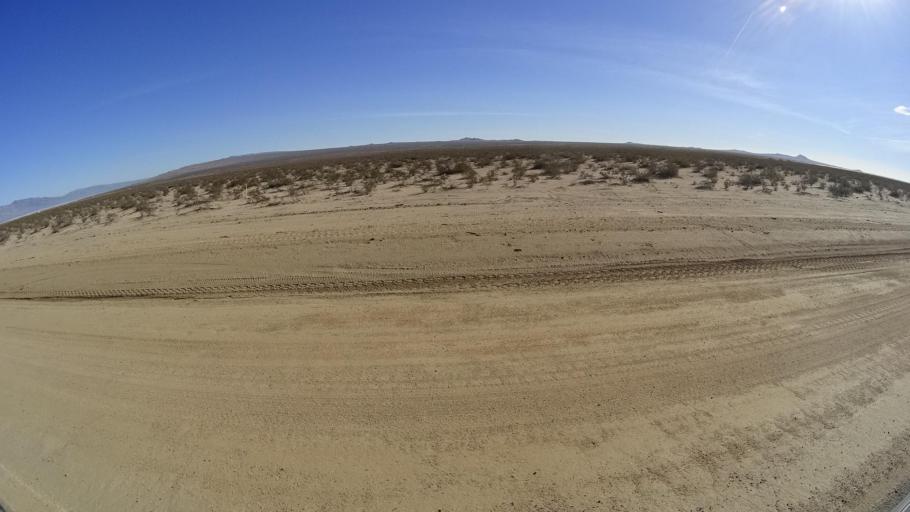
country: US
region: California
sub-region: Kern County
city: California City
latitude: 35.2079
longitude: -117.9858
